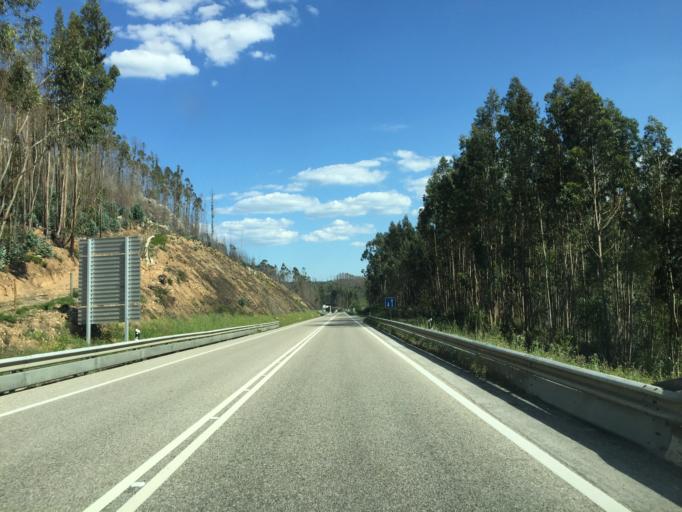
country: PT
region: Leiria
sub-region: Figueiro Dos Vinhos
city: Figueiro dos Vinhos
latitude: 39.9304
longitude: -8.3361
